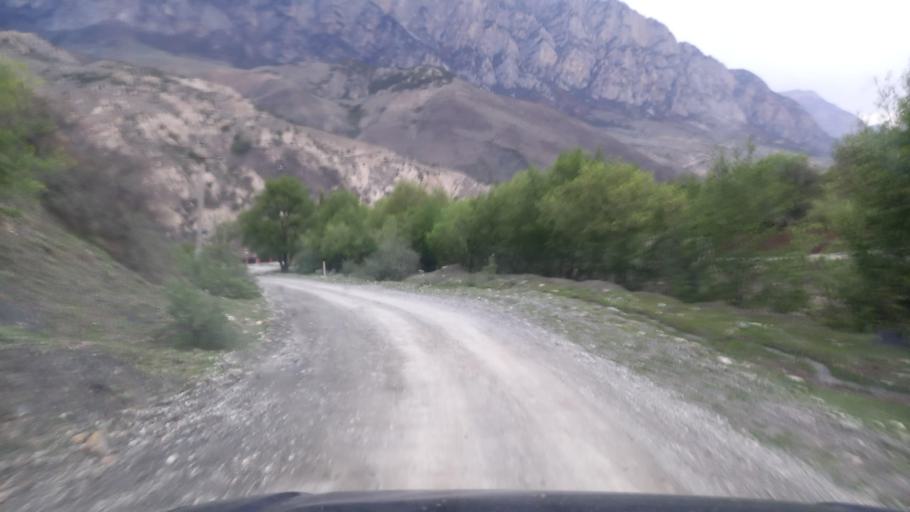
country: RU
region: North Ossetia
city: Mizur
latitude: 42.8576
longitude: 44.1489
